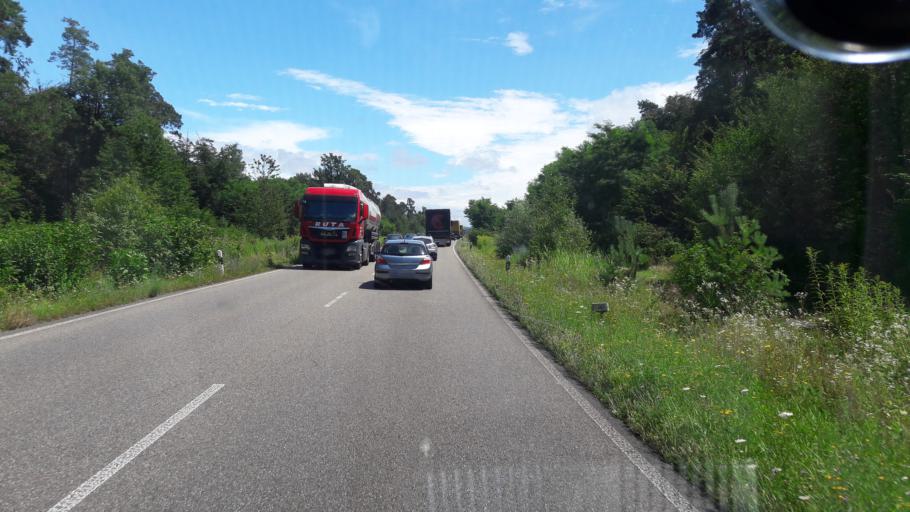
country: DE
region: Baden-Wuerttemberg
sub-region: Karlsruhe Region
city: Linkenheim-Hochstetten
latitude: 49.1455
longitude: 8.4539
